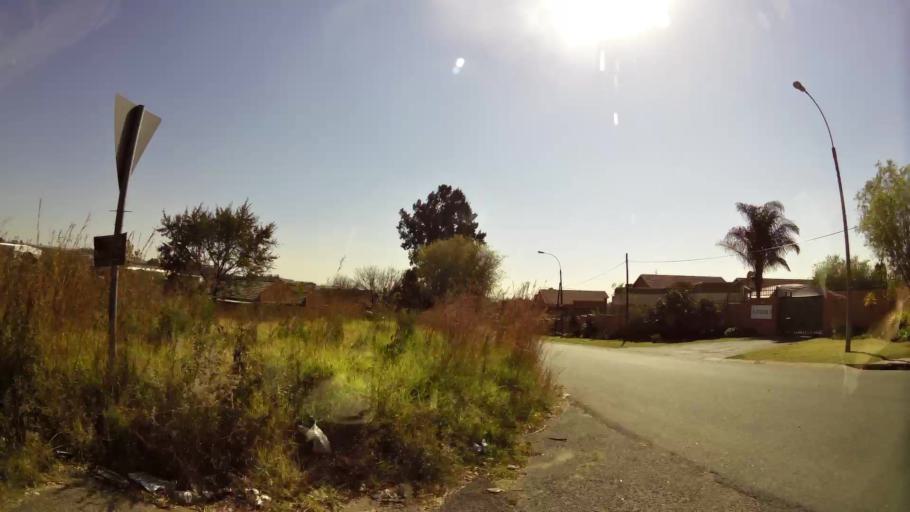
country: ZA
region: Gauteng
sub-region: City of Johannesburg Metropolitan Municipality
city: Modderfontein
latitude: -26.0683
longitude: 28.1979
